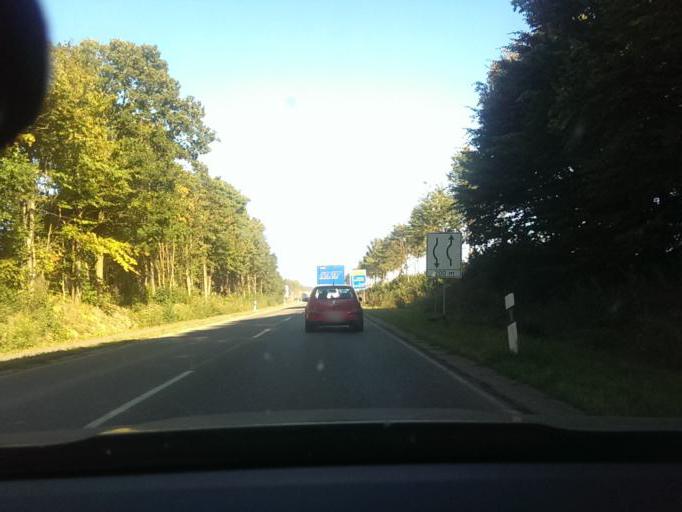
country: DE
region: Lower Saxony
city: Bockenem
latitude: 51.9459
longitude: 10.1355
